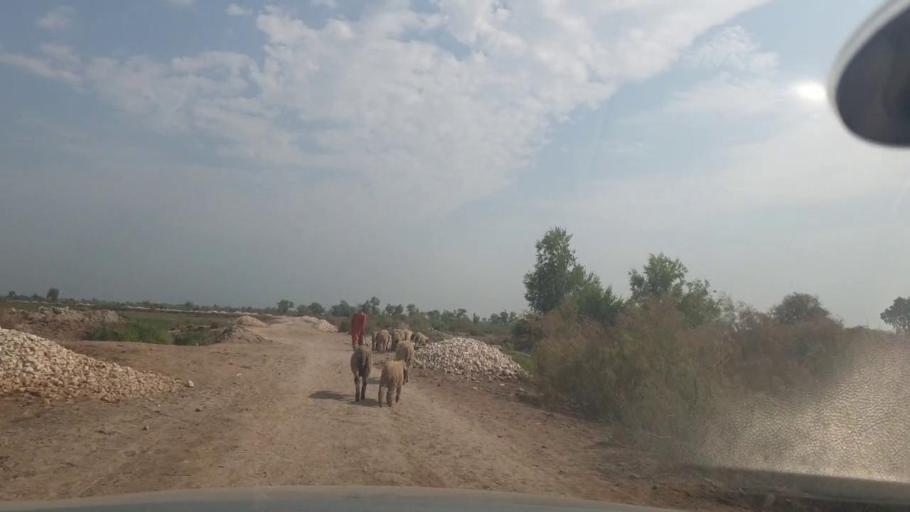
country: PK
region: Balochistan
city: Mehrabpur
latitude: 28.0754
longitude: 68.1002
